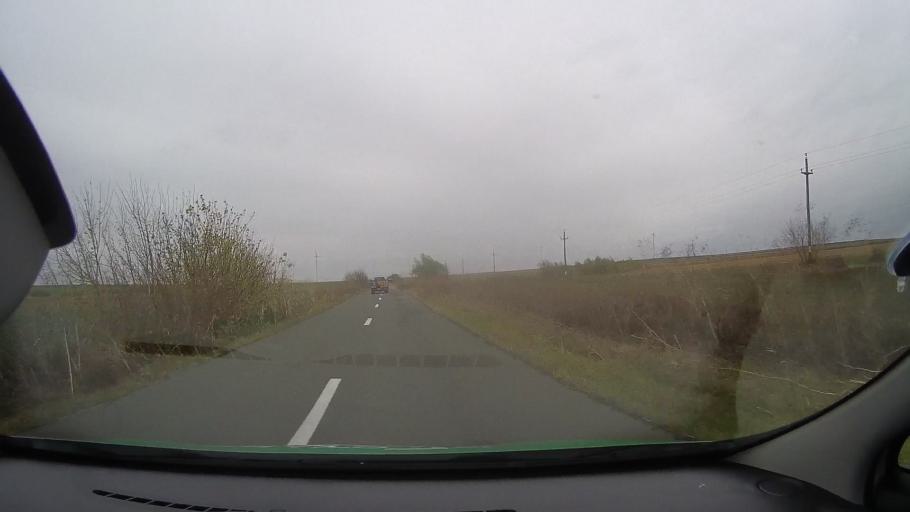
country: RO
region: Constanta
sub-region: Comuna Targusor
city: Targusor
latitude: 44.4690
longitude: 28.3901
